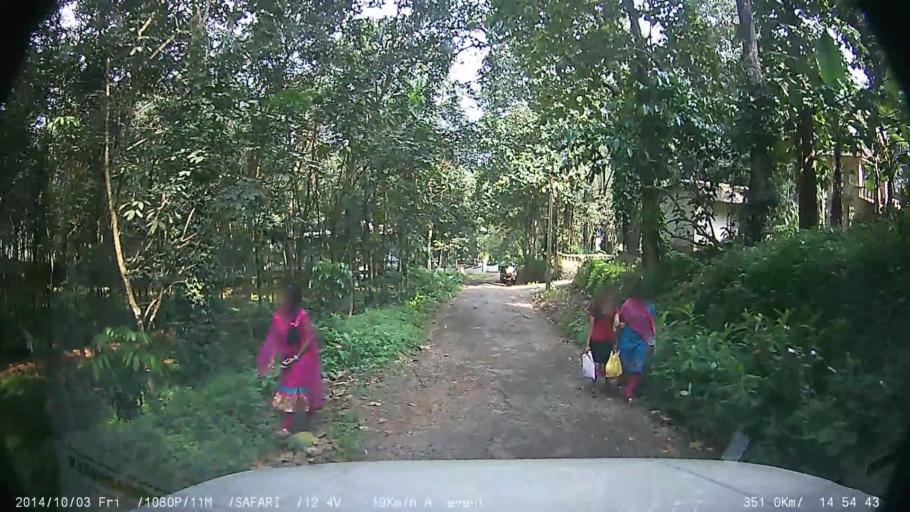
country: IN
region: Kerala
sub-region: Kottayam
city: Palackattumala
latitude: 9.7841
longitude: 76.5759
